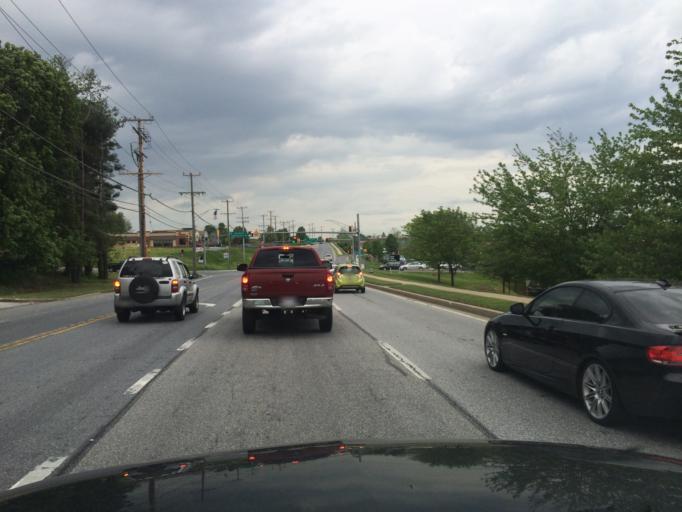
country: US
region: Maryland
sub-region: Carroll County
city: Eldersburg
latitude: 39.4075
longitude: -76.9504
